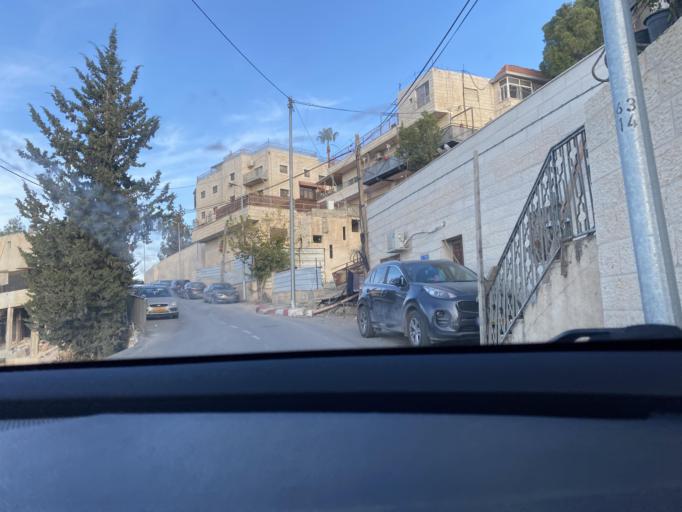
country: PS
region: West Bank
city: Ash Shaykh Sa`d
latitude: 31.7378
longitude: 35.2443
